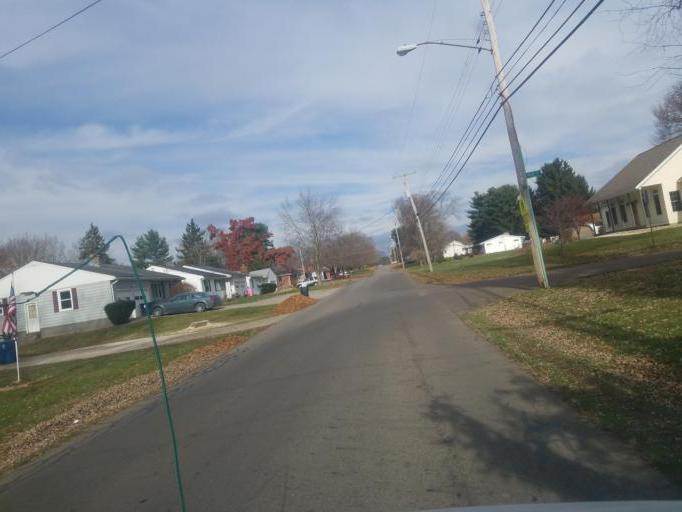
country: US
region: Ohio
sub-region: Knox County
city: Mount Vernon
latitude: 40.4077
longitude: -82.4889
